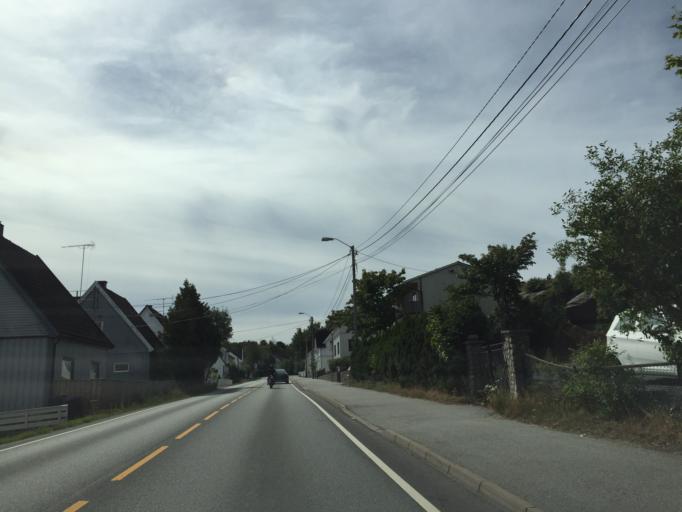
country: NO
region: Ostfold
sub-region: Fredrikstad
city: Fredrikstad
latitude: 59.1970
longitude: 10.9420
